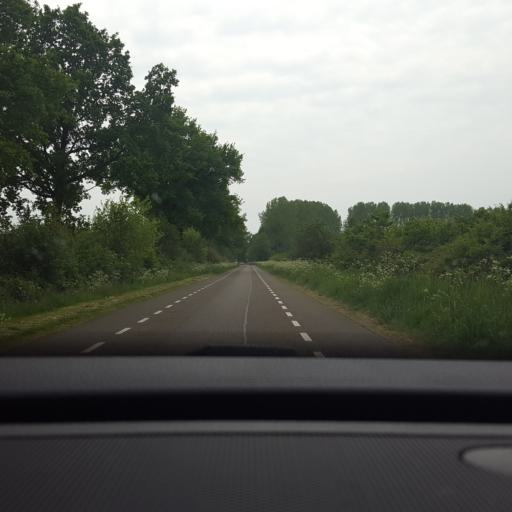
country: NL
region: Gelderland
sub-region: Gemeente Lochem
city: Barchem
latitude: 52.0486
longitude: 6.4483
